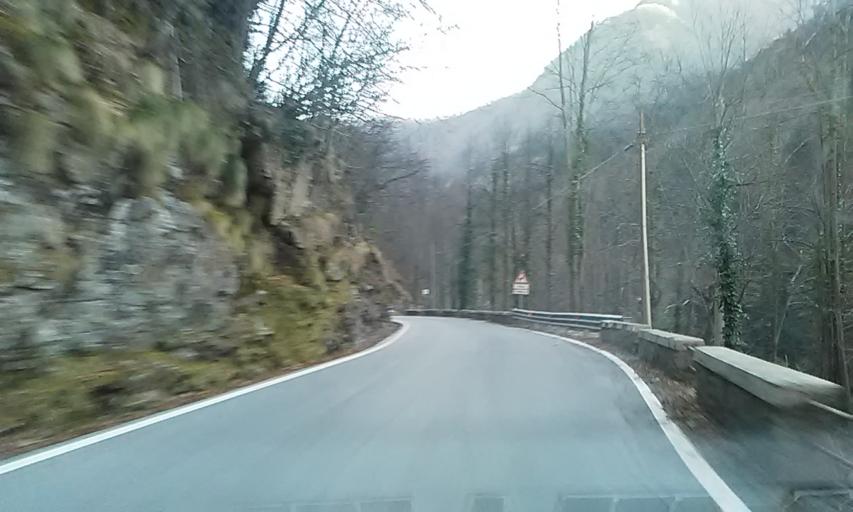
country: IT
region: Piedmont
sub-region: Provincia di Vercelli
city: Boccioleto
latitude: 45.8310
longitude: 8.0938
